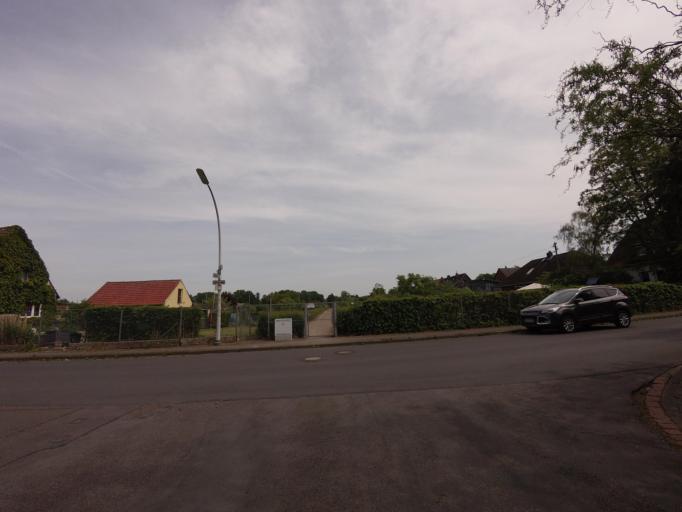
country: DE
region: Lower Saxony
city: Braunschweig
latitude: 52.3059
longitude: 10.5298
